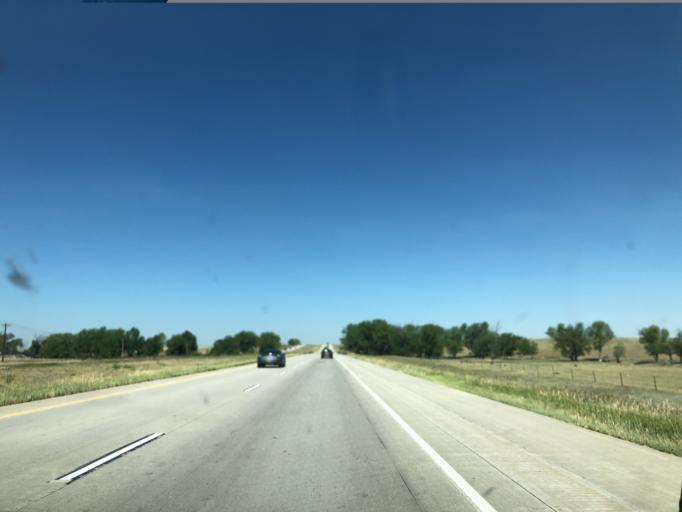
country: US
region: Colorado
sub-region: Arapahoe County
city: Byers
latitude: 39.6928
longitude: -104.1423
